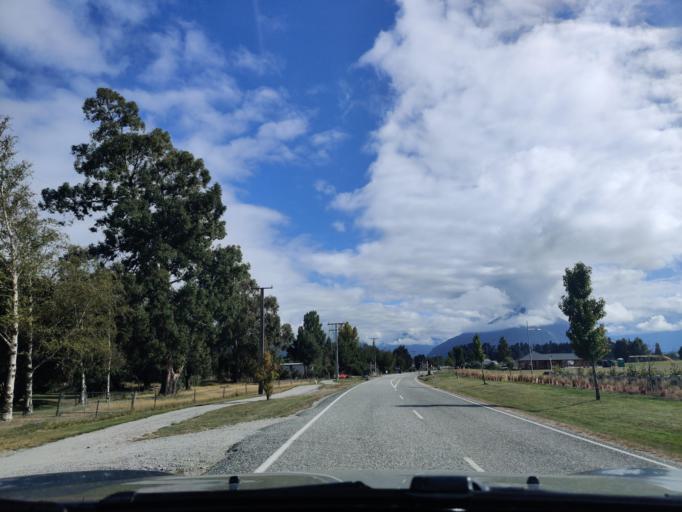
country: NZ
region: Otago
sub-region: Queenstown-Lakes District
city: Queenstown
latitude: -44.8561
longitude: 168.3910
